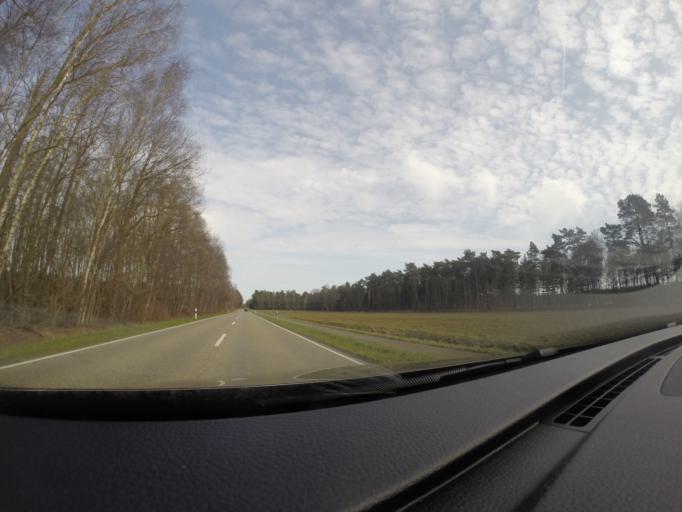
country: DE
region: North Rhine-Westphalia
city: Stadtlohn
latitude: 52.0487
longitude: 6.8996
